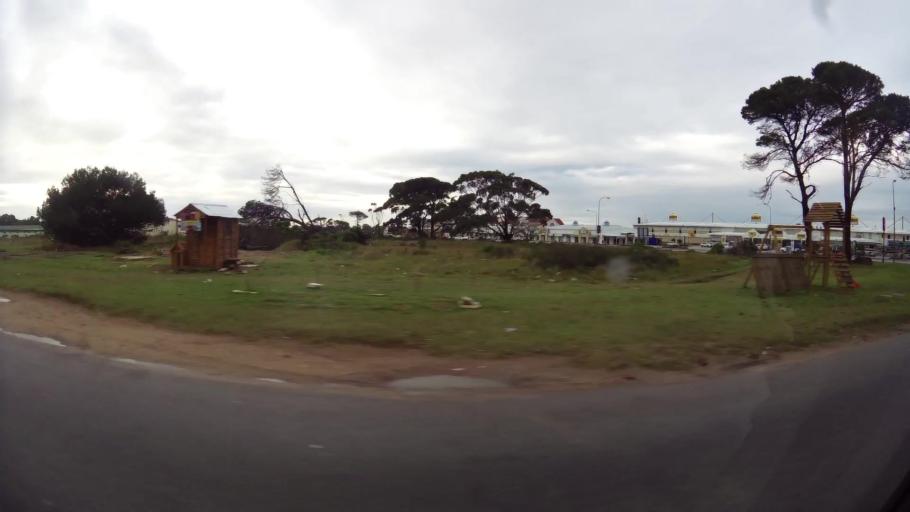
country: ZA
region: Eastern Cape
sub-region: Nelson Mandela Bay Metropolitan Municipality
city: Port Elizabeth
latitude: -33.9908
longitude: 25.5522
